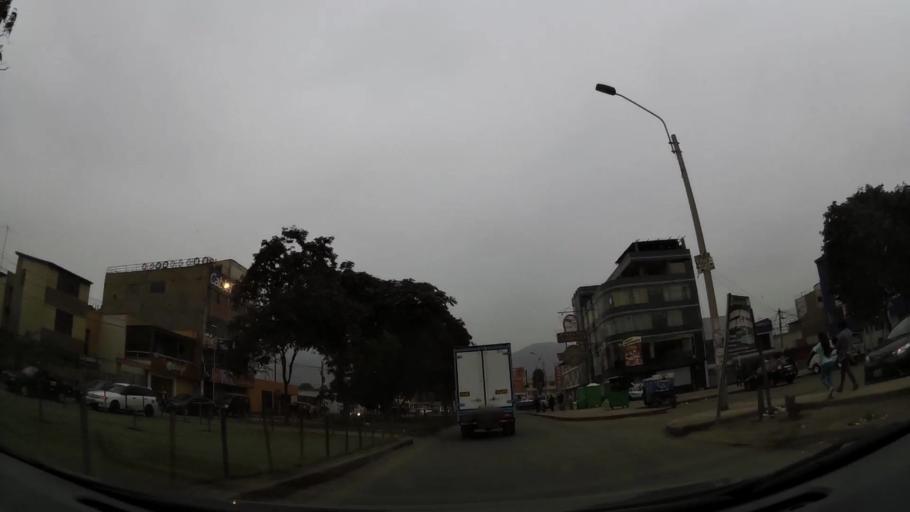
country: PE
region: Lima
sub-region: Lima
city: Urb. Santo Domingo
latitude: -11.9004
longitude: -77.0409
